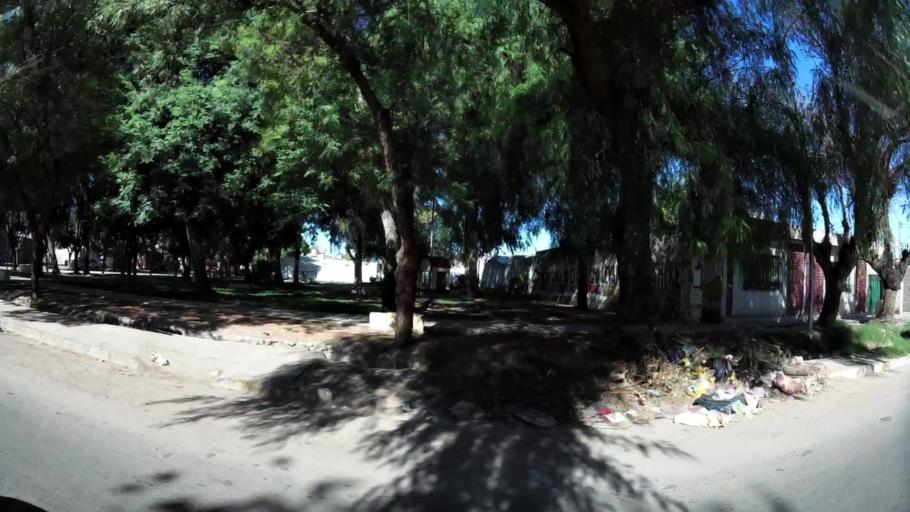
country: AR
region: Mendoza
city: Las Heras
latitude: -32.8488
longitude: -68.8206
